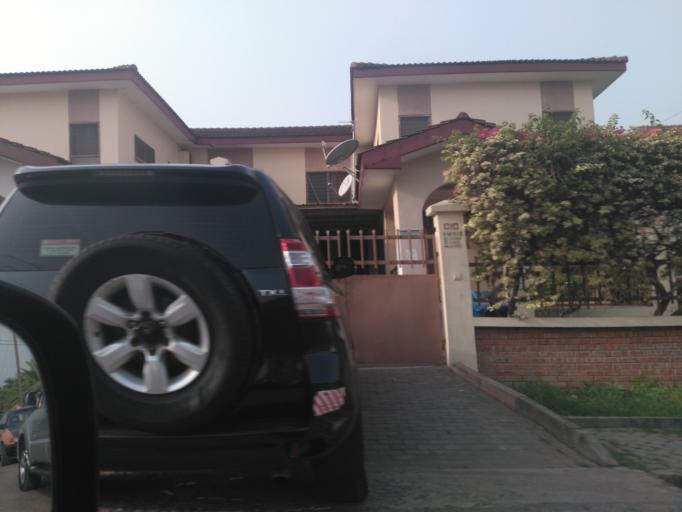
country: GH
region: Greater Accra
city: Accra
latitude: 5.6057
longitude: -0.1963
